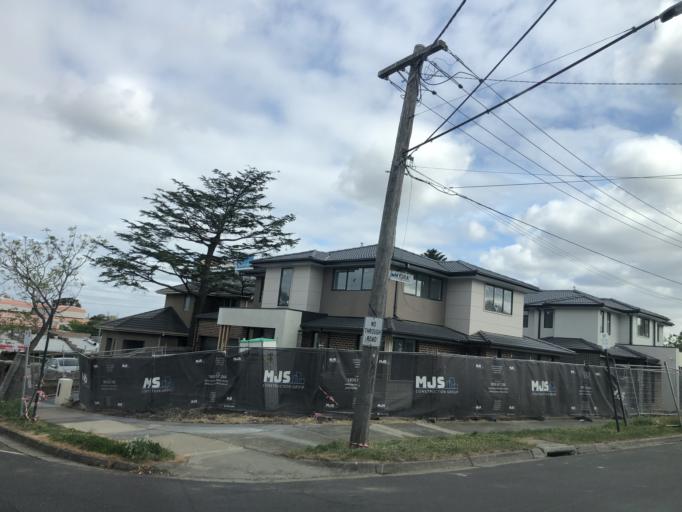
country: AU
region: Victoria
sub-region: Monash
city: Chadstone
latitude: -37.8756
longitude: 145.0928
